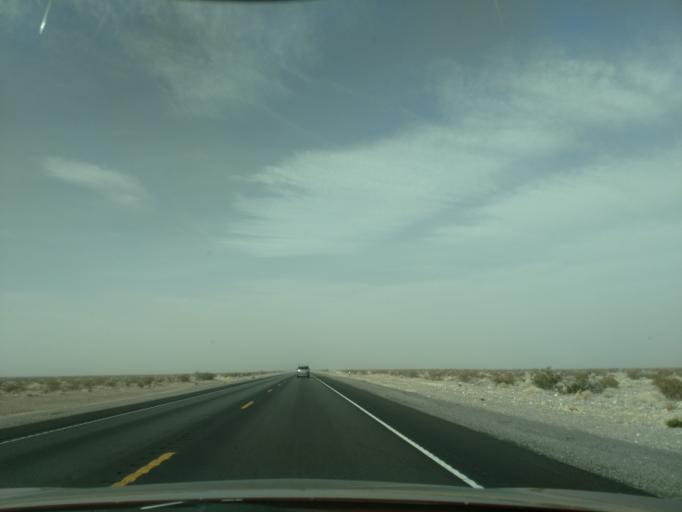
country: US
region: Nevada
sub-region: Nye County
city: Beatty
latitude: 36.6345
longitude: -116.3625
